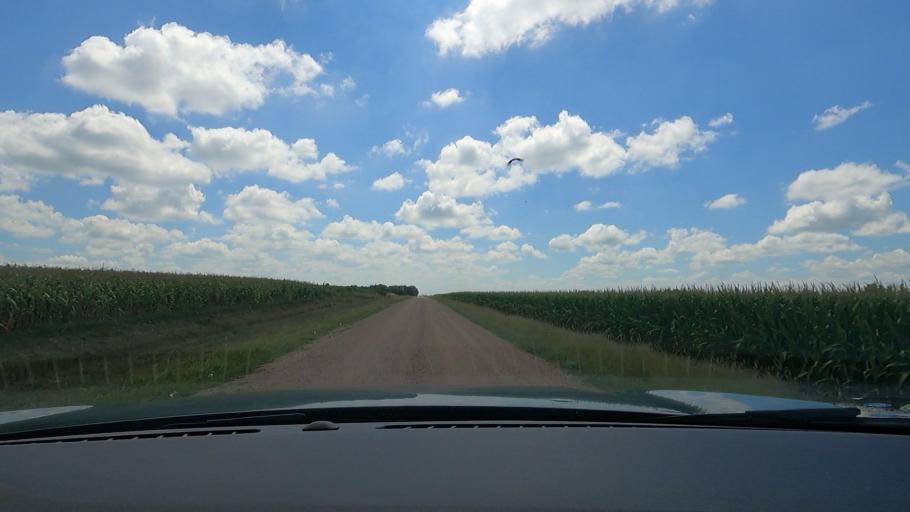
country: US
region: Nebraska
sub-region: Saunders County
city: Wahoo
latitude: 41.2716
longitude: -96.5418
